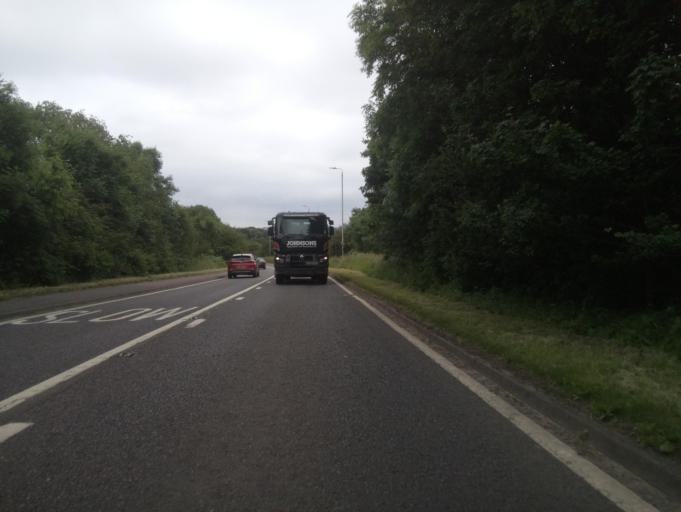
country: GB
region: England
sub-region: Leicestershire
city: Melton Mowbray
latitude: 52.7647
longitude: -0.9199
